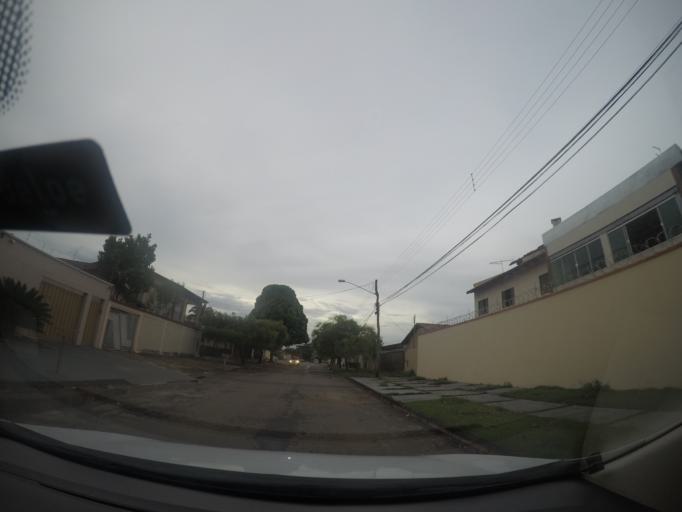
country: BR
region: Goias
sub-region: Goiania
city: Goiania
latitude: -16.6388
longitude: -49.2409
